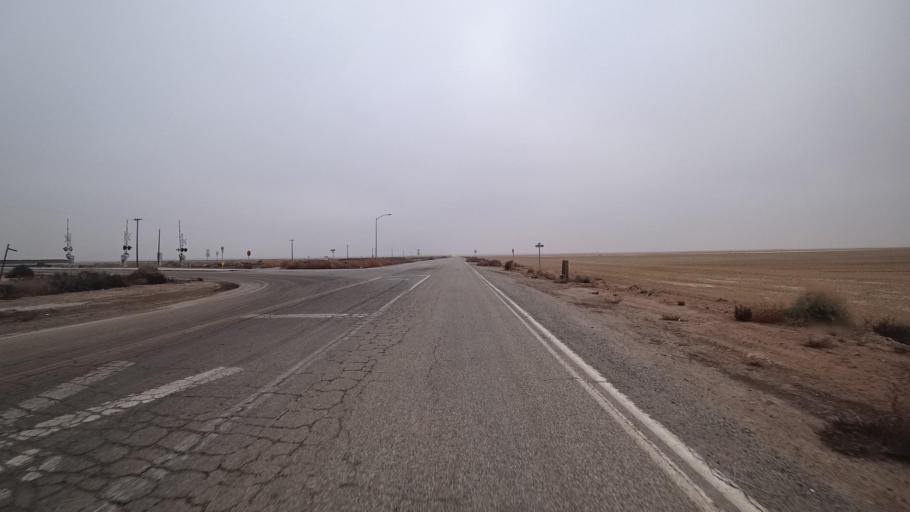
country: US
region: California
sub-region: Kern County
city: Maricopa
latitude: 35.1350
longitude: -119.2493
